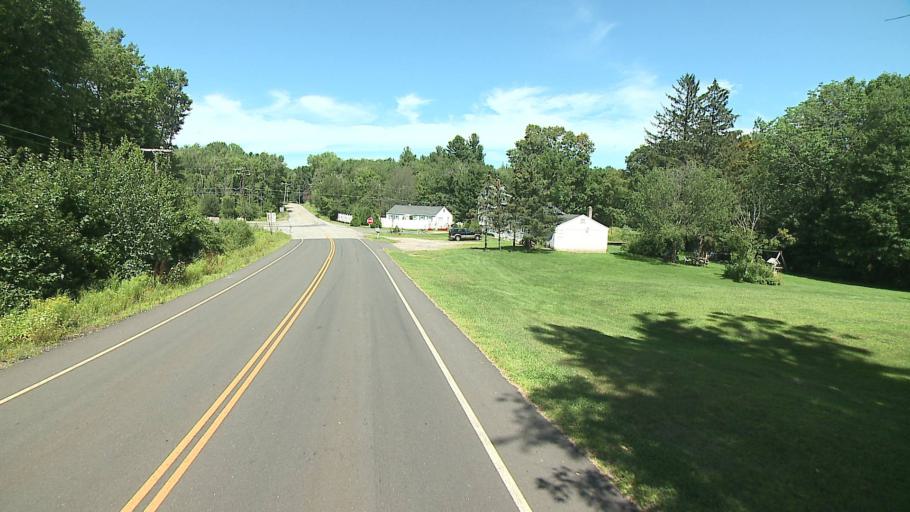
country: US
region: Connecticut
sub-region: Litchfield County
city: Winsted
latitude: 41.9954
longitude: -72.9799
